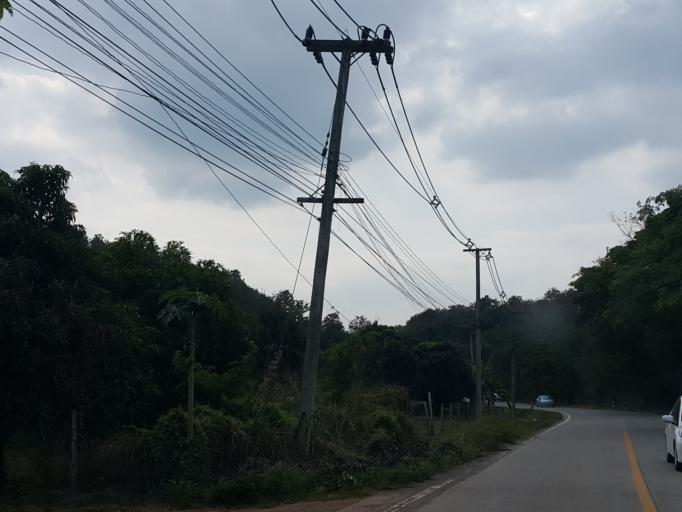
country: TH
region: Chiang Mai
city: Mae On
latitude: 18.8091
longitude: 99.2374
